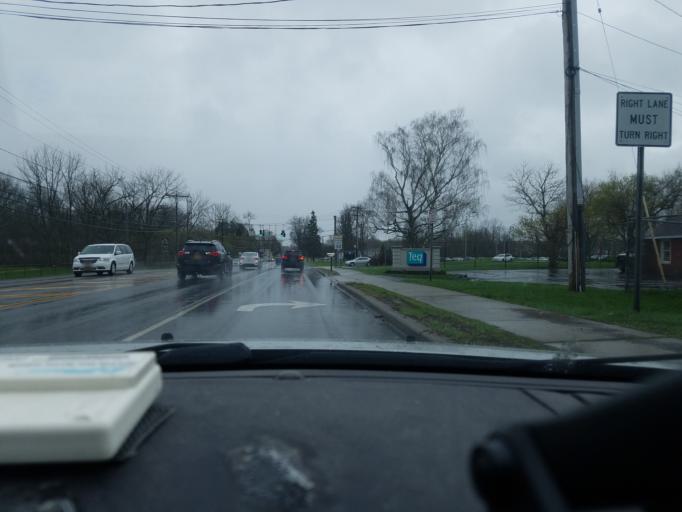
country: US
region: New York
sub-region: Onondaga County
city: North Syracuse
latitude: 43.1758
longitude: -76.1053
